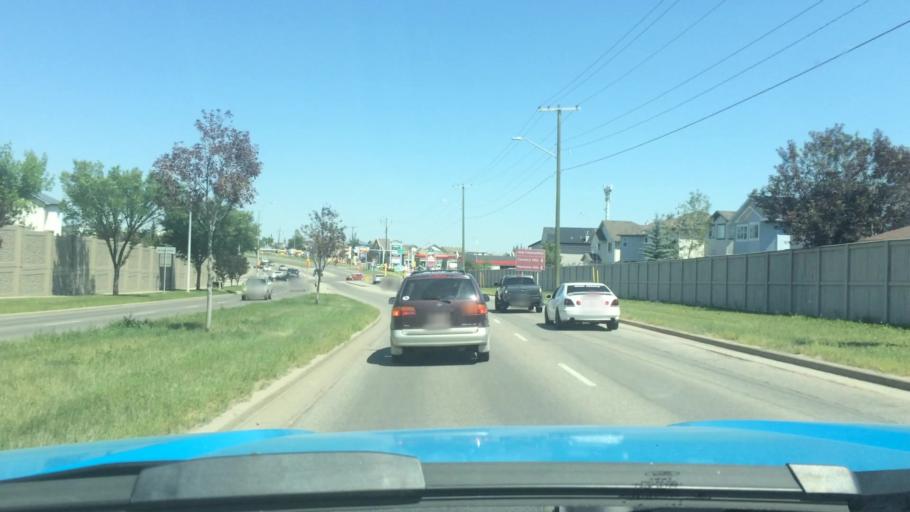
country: CA
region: Alberta
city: Calgary
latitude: 51.1478
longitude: -114.0759
